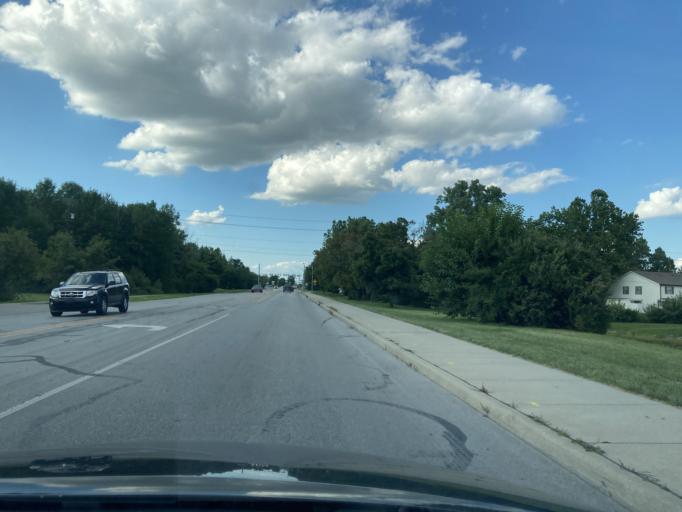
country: US
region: Indiana
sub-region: Boone County
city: Zionsville
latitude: 39.8771
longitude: -86.2444
